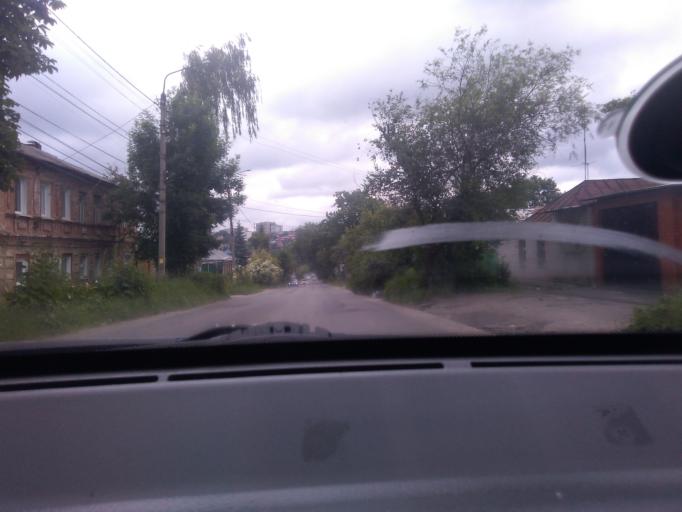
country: RU
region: Kursk
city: Kursk
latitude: 51.7289
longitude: 36.1741
